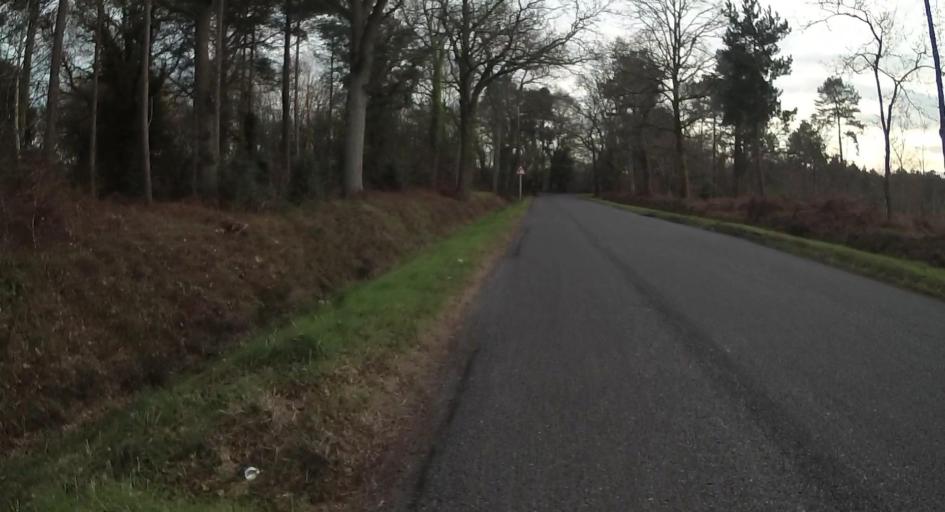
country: GB
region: England
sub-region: West Berkshire
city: Theale
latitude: 51.3979
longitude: -1.0880
